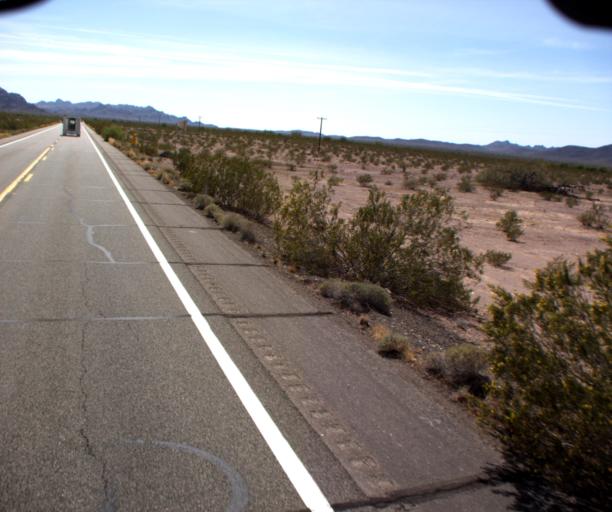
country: US
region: Arizona
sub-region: La Paz County
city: Quartzsite
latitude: 33.3348
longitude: -114.2170
